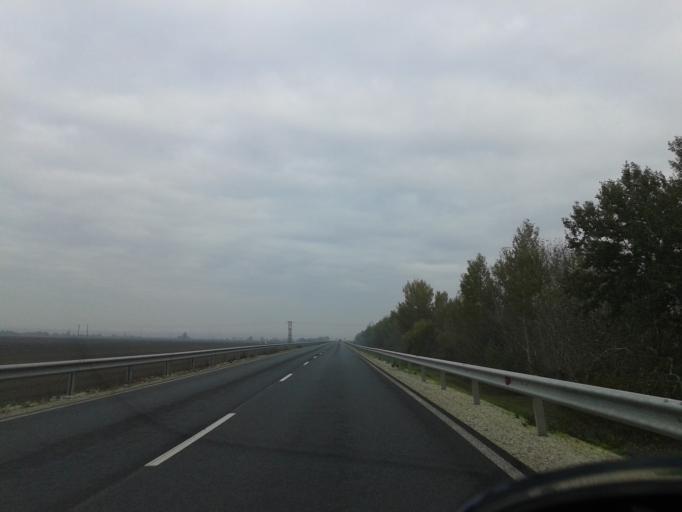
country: HU
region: Fejer
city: Ercsi
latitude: 47.2098
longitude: 18.8838
